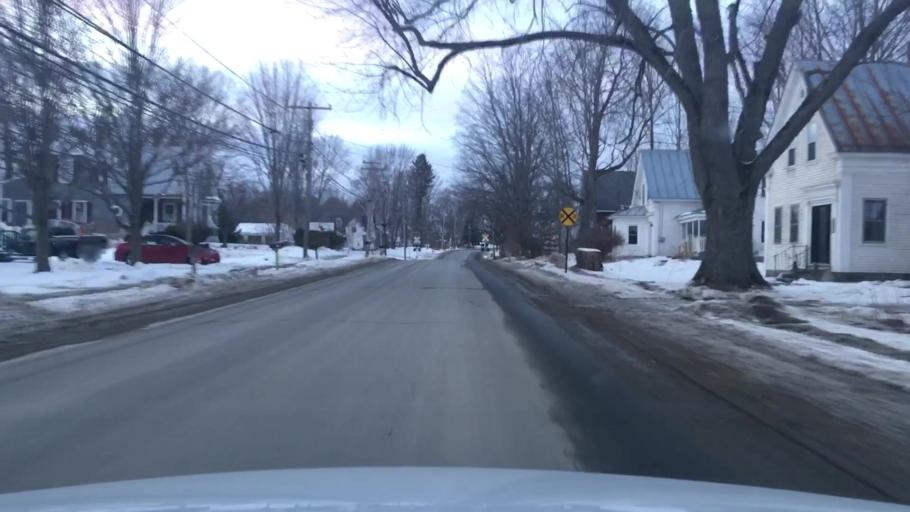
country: US
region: Maine
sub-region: Kennebec County
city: Clinton
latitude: 44.6393
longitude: -69.5037
